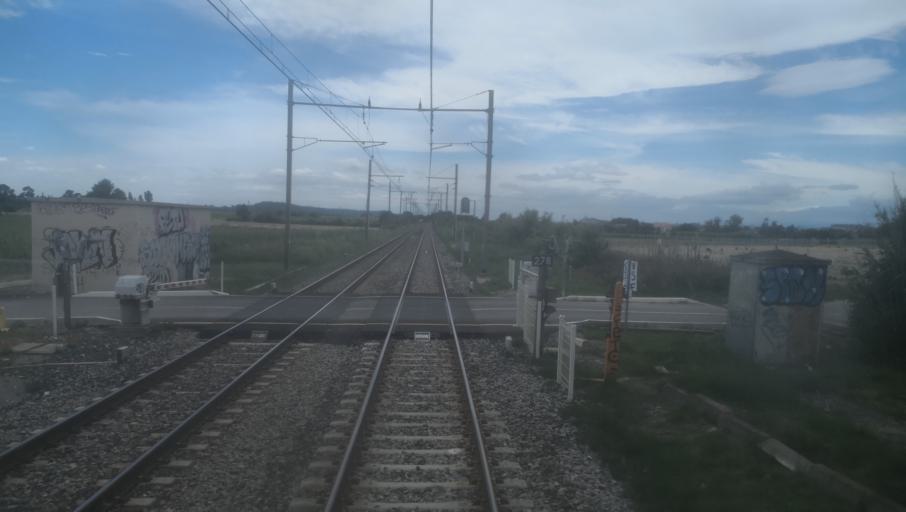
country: FR
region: Languedoc-Roussillon
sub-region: Departement de l'Herault
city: Colombiers
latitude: 43.3329
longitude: 3.1717
